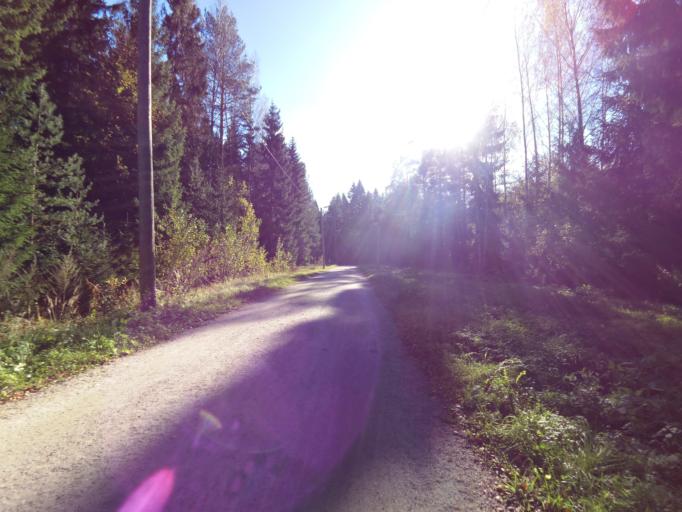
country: FI
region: Uusimaa
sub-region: Helsinki
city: Kauniainen
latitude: 60.1859
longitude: 24.6939
